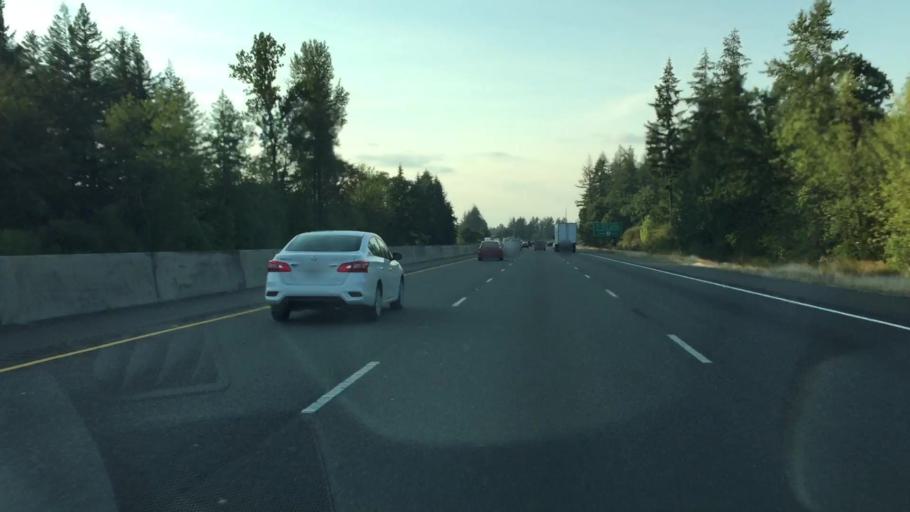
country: US
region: Washington
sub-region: Thurston County
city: Grand Mound
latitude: 46.7874
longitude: -123.0062
